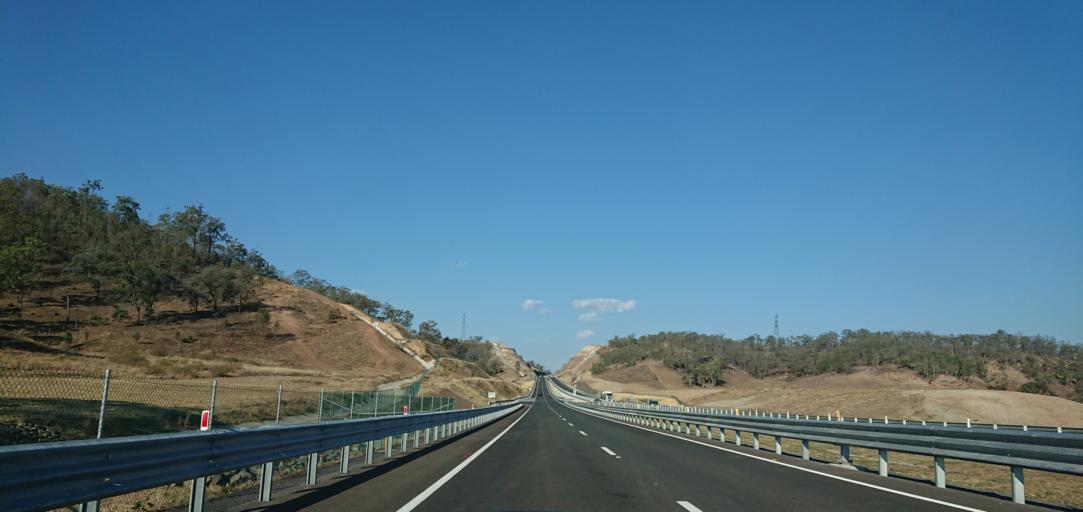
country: AU
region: Queensland
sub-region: Toowoomba
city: East Toowoomba
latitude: -27.5153
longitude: 152.0293
